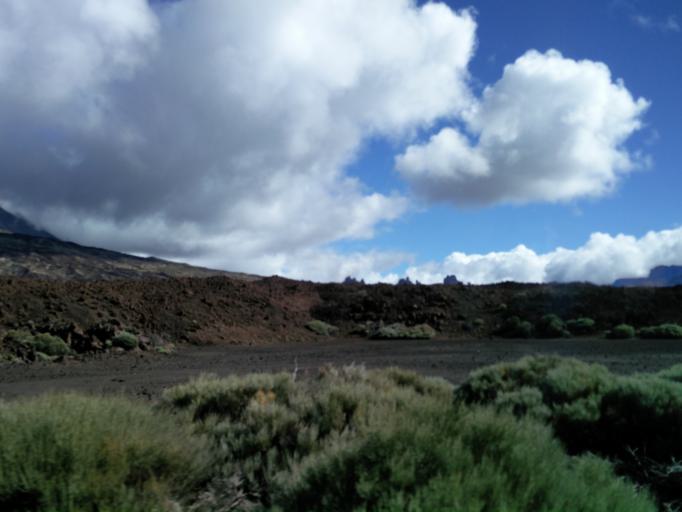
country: ES
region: Canary Islands
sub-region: Provincia de Santa Cruz de Tenerife
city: Vilaflor
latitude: 28.2145
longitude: -16.6656
